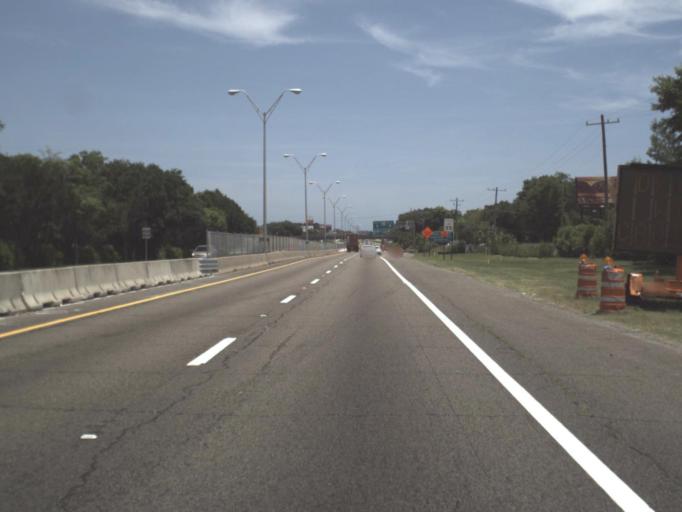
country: US
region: Florida
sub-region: Duval County
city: Jacksonville
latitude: 30.3272
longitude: -81.6095
